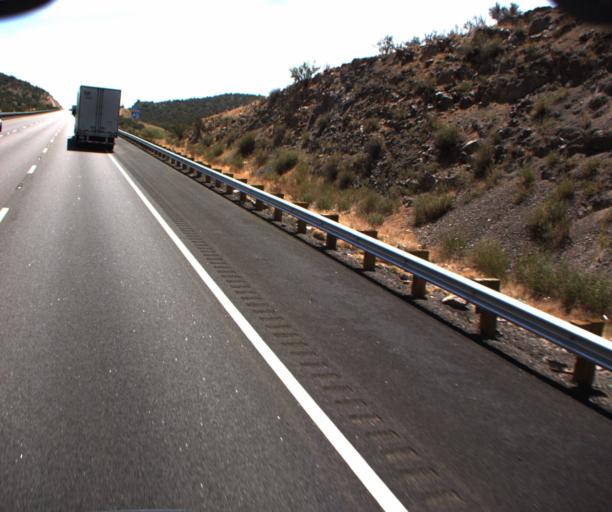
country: US
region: Arizona
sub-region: Mohave County
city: Peach Springs
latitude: 35.1874
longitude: -113.4157
